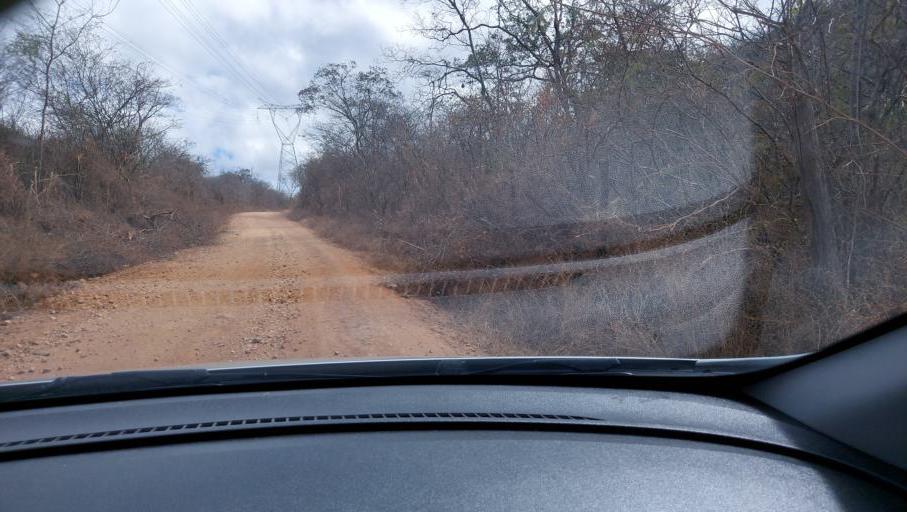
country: BR
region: Bahia
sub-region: Oliveira Dos Brejinhos
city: Beira Rio
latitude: -12.0906
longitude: -42.5433
